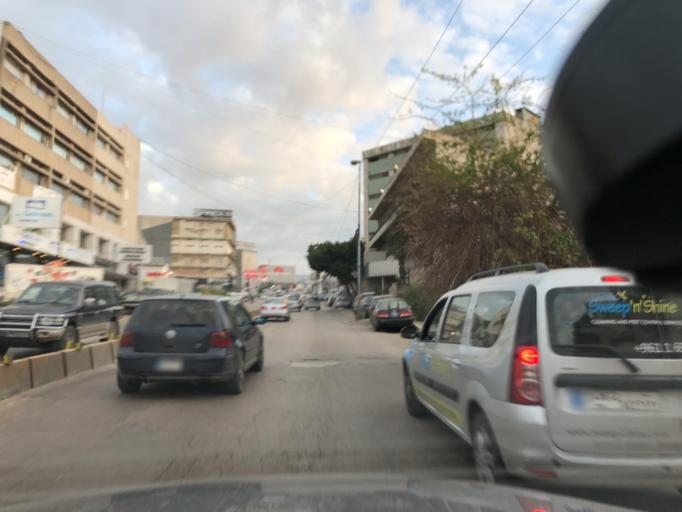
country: LB
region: Mont-Liban
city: Baabda
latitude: 33.8658
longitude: 35.5456
